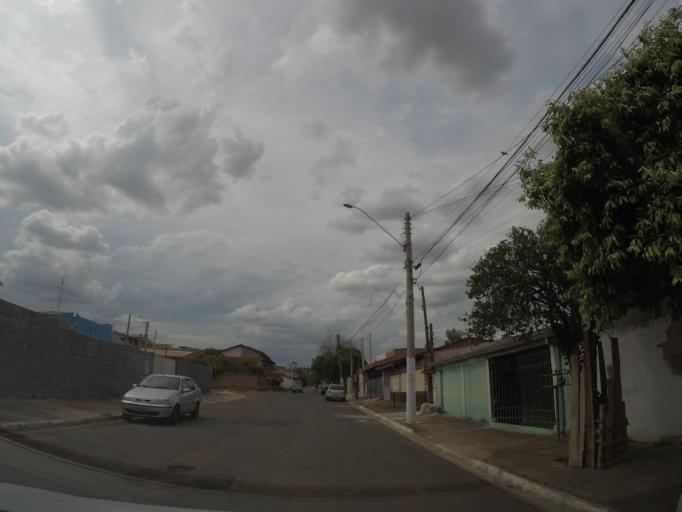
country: BR
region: Sao Paulo
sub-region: Sumare
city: Sumare
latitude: -22.8132
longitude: -47.2365
